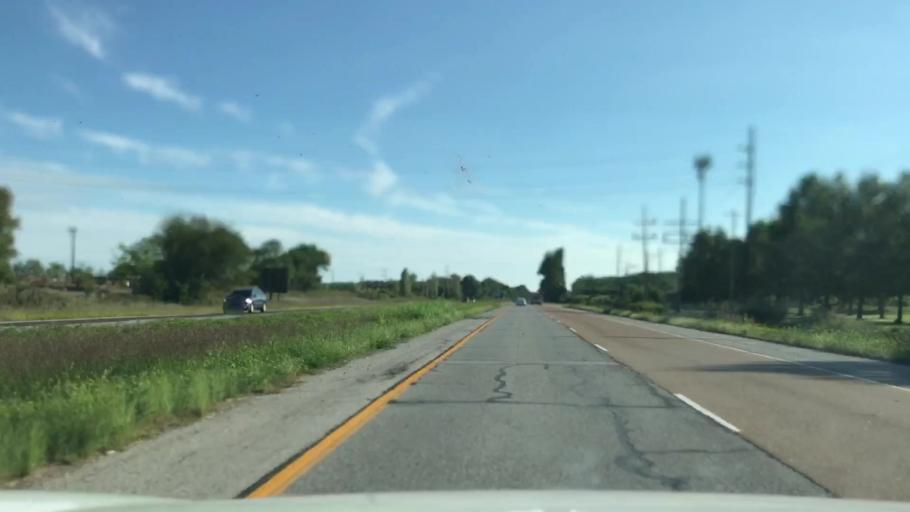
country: US
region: Illinois
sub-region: Madison County
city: Hartford
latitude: 38.8007
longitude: -90.1006
